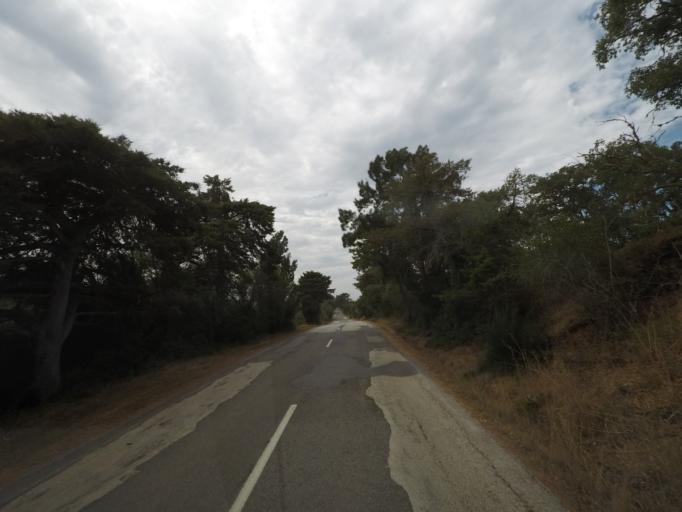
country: PT
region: Faro
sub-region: Aljezur
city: Aljezur
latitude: 37.2554
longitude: -8.8164
